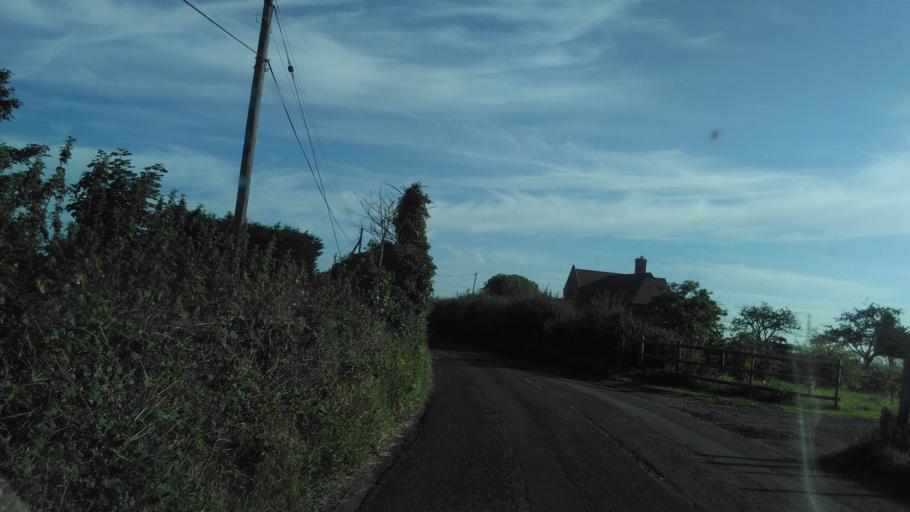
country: GB
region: England
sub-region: Kent
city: Dunkirk
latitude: 51.3294
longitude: 0.9478
